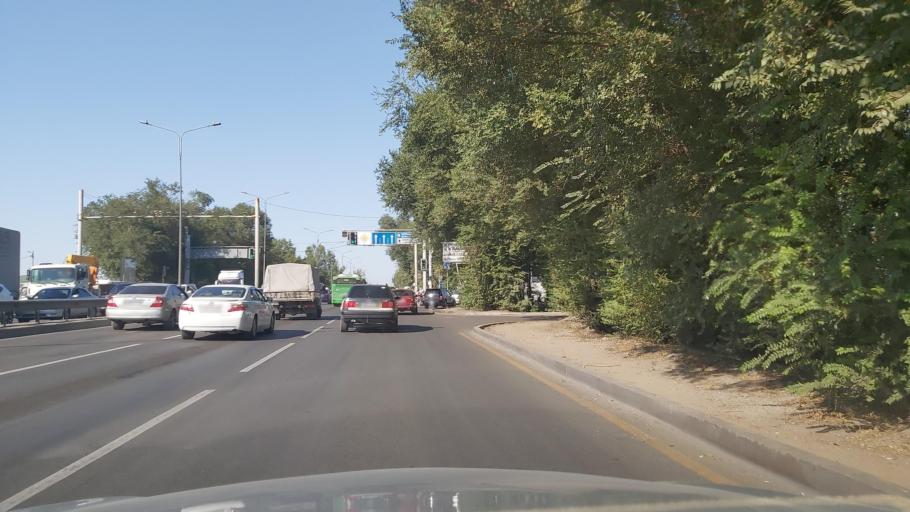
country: KZ
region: Almaty Oblysy
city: Pervomayskiy
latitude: 43.3244
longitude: 76.9071
